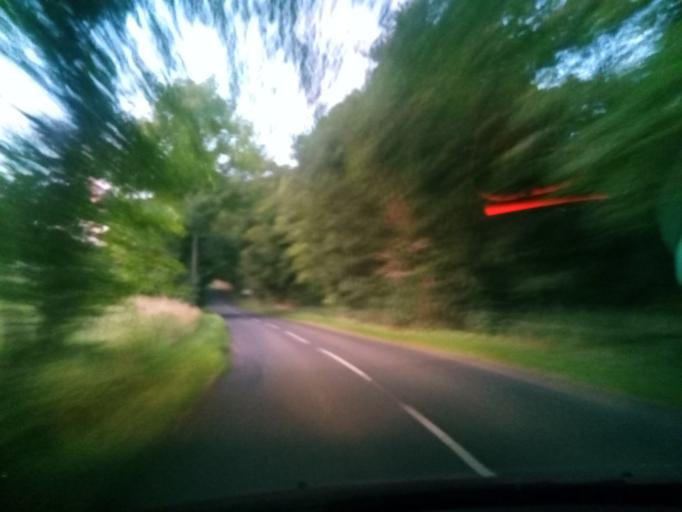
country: GB
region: England
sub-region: Northumberland
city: Wall
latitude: 55.0261
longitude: -2.1487
